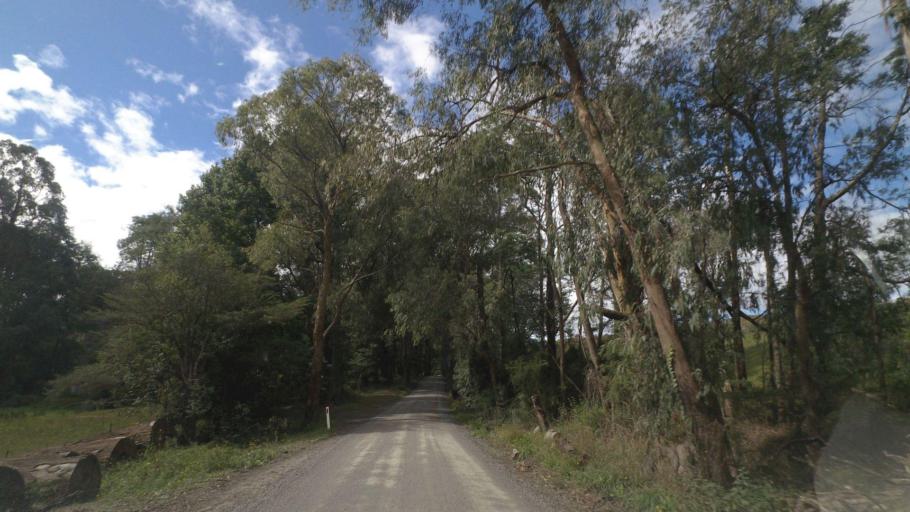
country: AU
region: Victoria
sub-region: Cardinia
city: Gembrook
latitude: -37.8853
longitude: 145.6021
